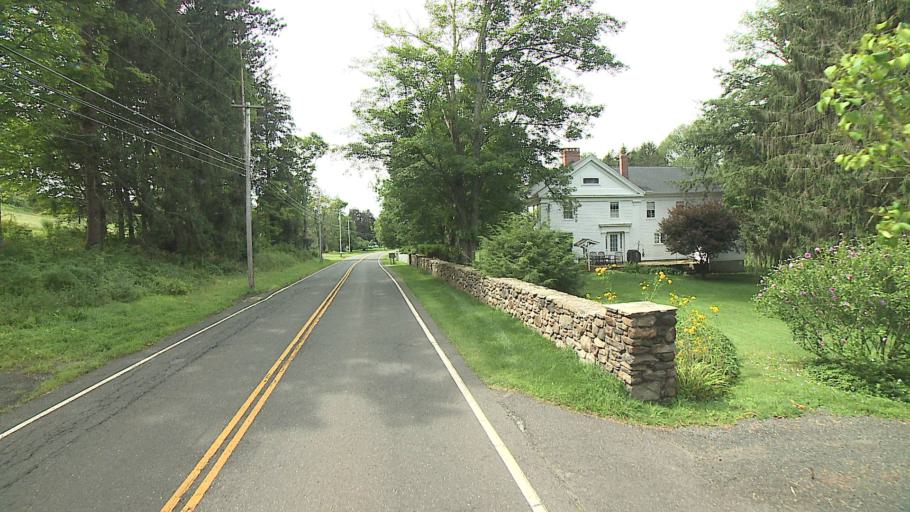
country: US
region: Connecticut
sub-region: Litchfield County
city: Woodbury
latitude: 41.5606
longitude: -73.3037
